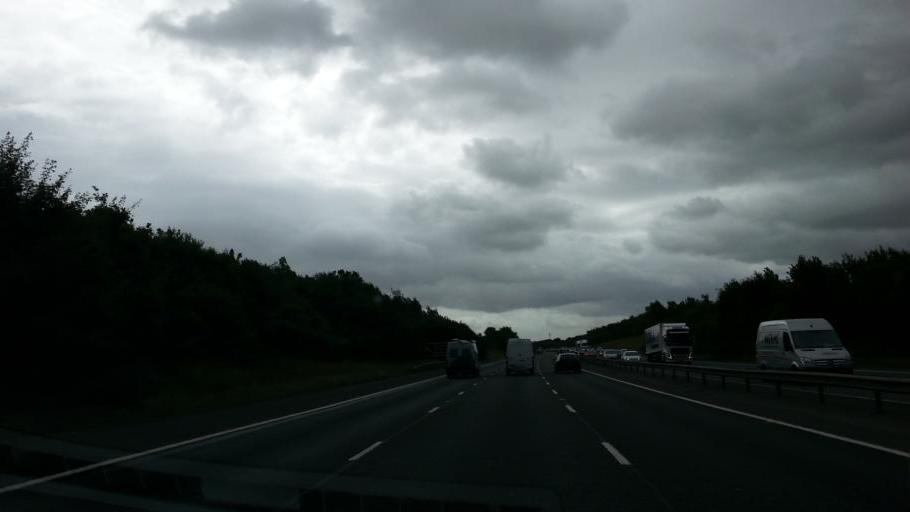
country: GB
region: England
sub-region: Warwickshire
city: Harbury
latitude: 52.2024
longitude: -1.4738
